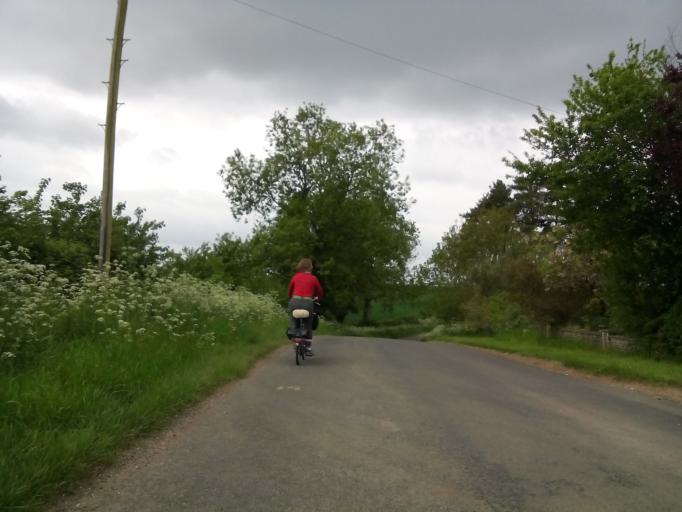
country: GB
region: England
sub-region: District of Rutland
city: South Luffenham
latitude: 52.5266
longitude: -0.5637
